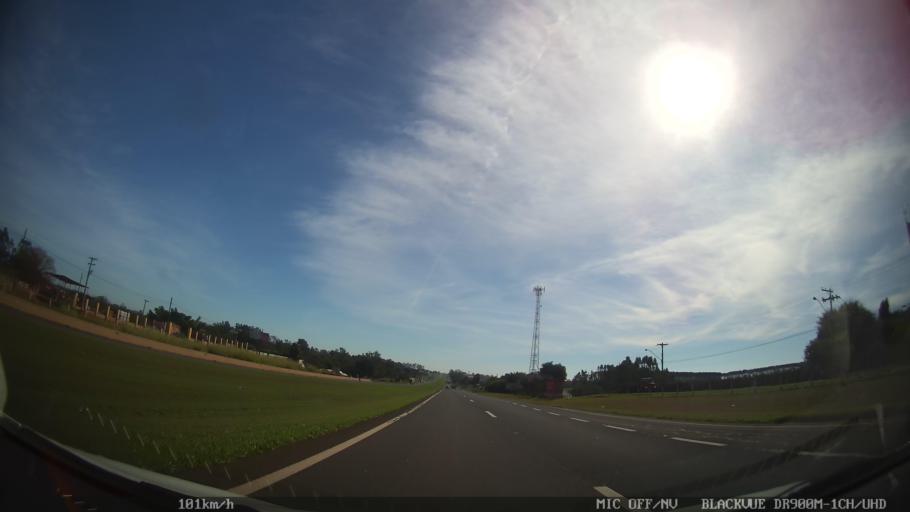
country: BR
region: Sao Paulo
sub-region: Leme
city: Leme
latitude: -22.2218
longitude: -47.3918
